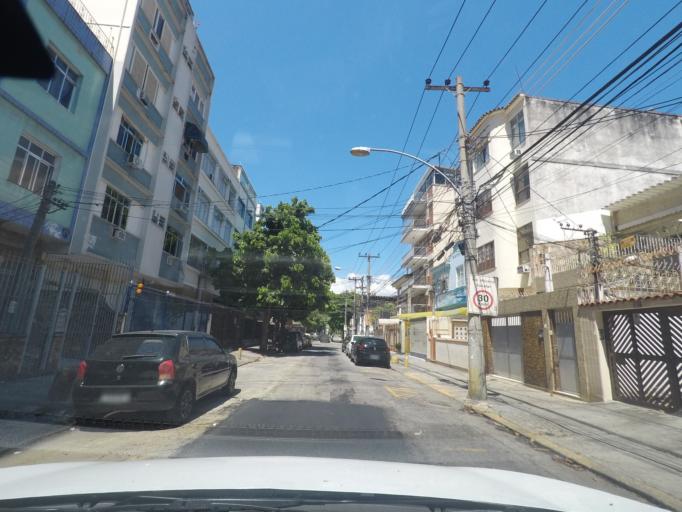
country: BR
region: Rio de Janeiro
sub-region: Rio De Janeiro
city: Rio de Janeiro
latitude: -22.9184
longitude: -43.2386
